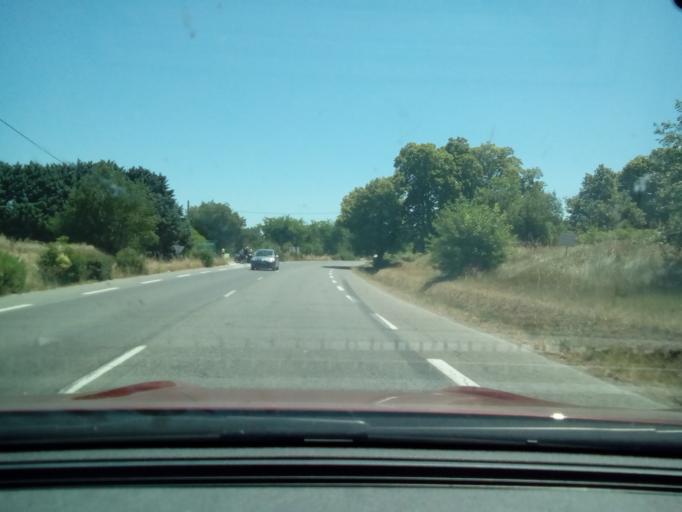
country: FR
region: Provence-Alpes-Cote d'Azur
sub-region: Departement des Bouches-du-Rhone
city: Chateauneuf-le-Rouge
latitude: 43.4794
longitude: 5.5576
